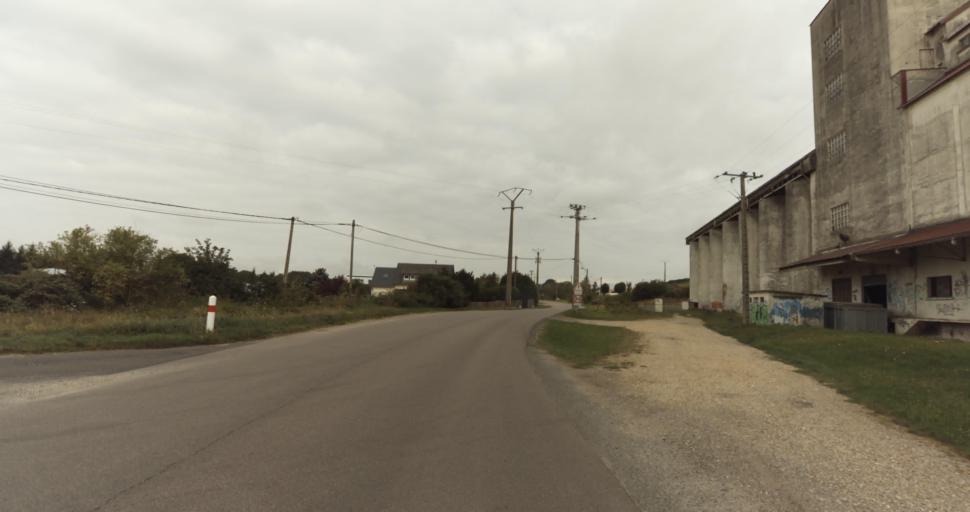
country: FR
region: Haute-Normandie
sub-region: Departement de l'Eure
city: Bueil
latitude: 48.9201
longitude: 1.4508
